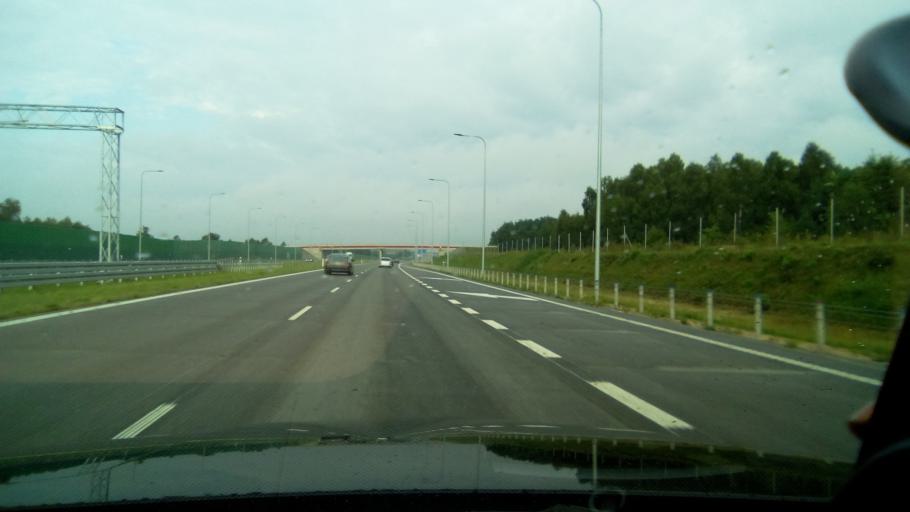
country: PL
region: Silesian Voivodeship
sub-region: Powiat czestochowski
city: Mykanow
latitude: 50.8758
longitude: 19.1362
